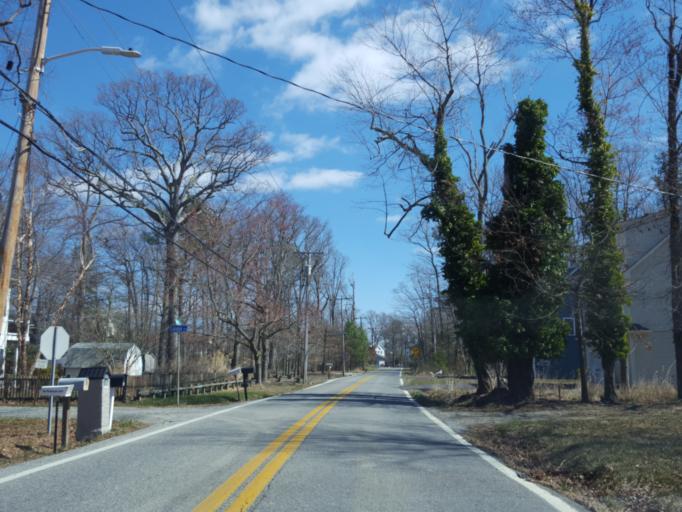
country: US
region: Maryland
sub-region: Calvert County
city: North Beach
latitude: 38.7272
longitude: -76.5311
